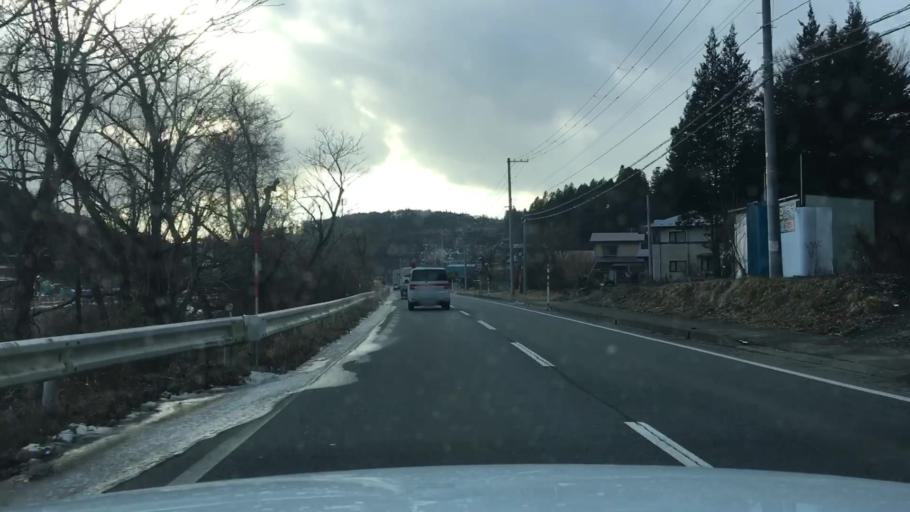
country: JP
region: Iwate
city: Morioka-shi
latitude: 39.6751
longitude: 141.2173
